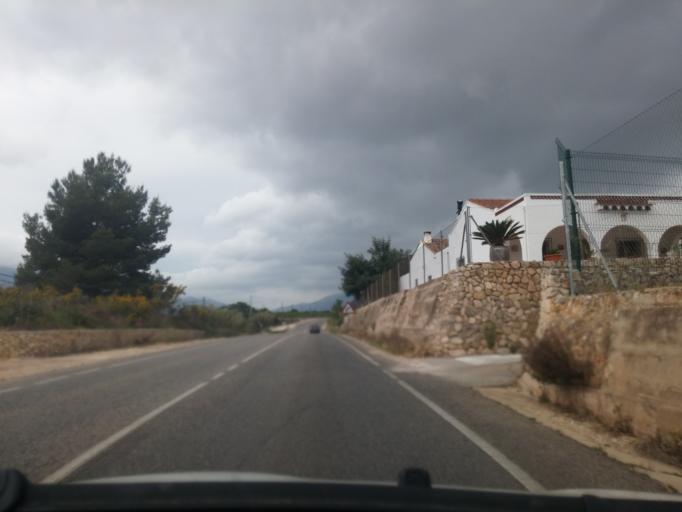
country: ES
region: Valencia
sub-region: Provincia de Alicante
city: Jalon
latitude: 38.7465
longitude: -0.0253
